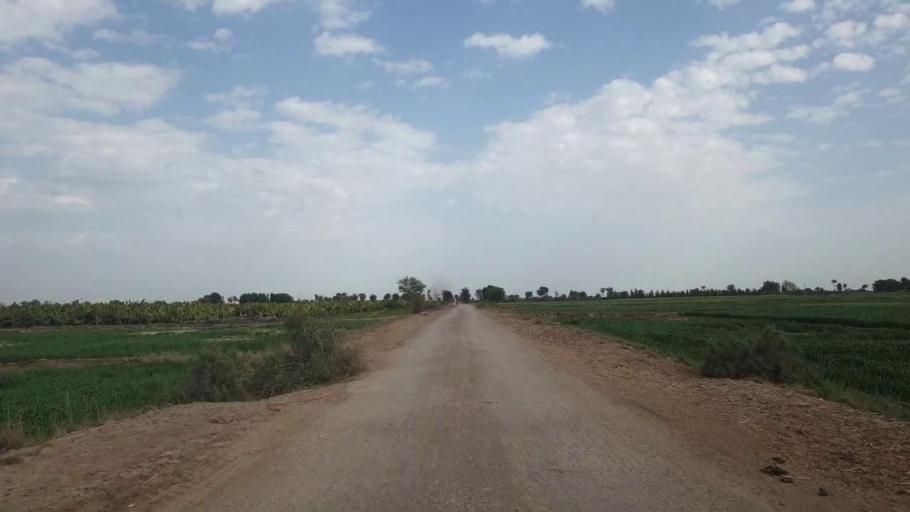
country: PK
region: Sindh
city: Shahdadpur
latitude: 25.9655
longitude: 68.4711
